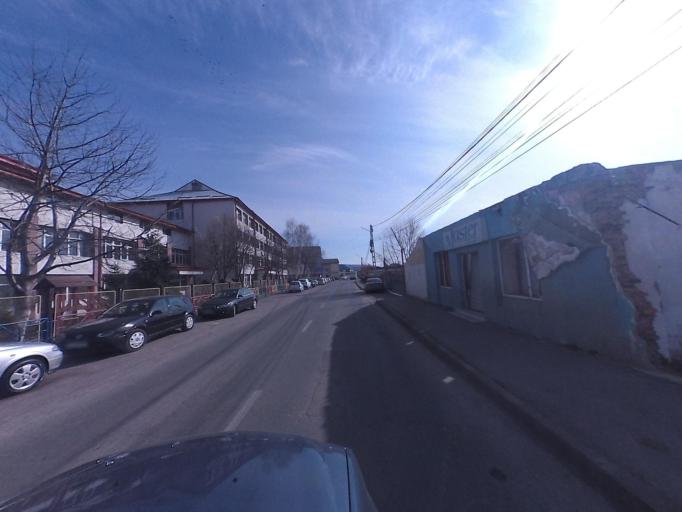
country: RO
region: Neamt
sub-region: Oras Targu Neamt
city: Targu Neamt
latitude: 47.2043
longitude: 26.3610
